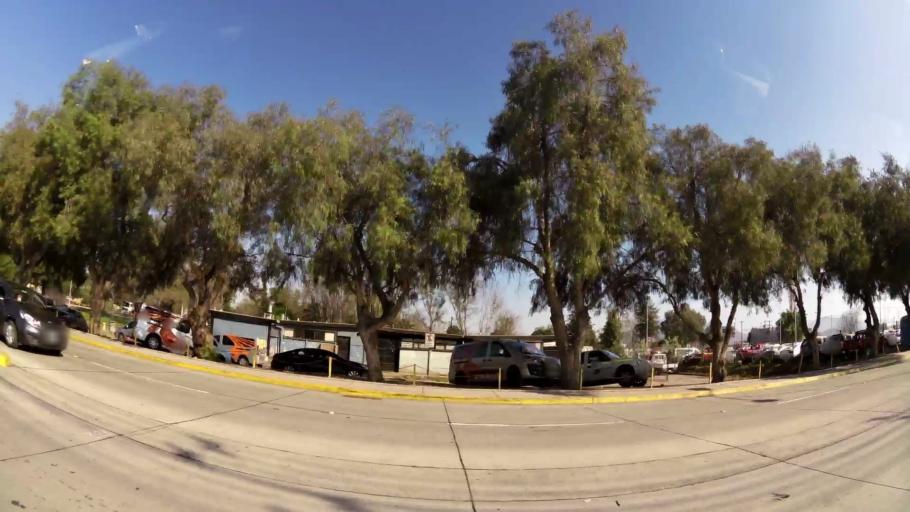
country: CL
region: Santiago Metropolitan
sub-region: Provincia de Santiago
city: Lo Prado
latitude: -33.4024
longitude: -70.7927
